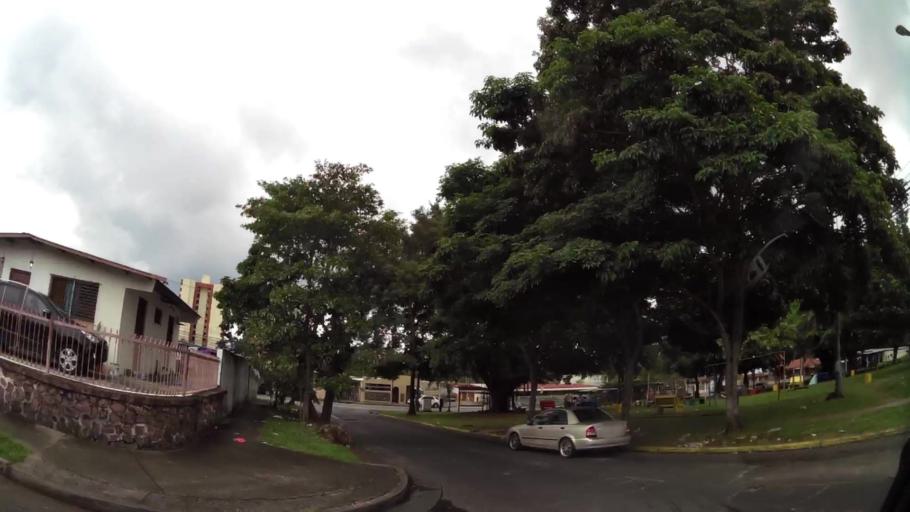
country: PA
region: Panama
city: Tocumen
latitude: 9.0616
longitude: -79.4164
